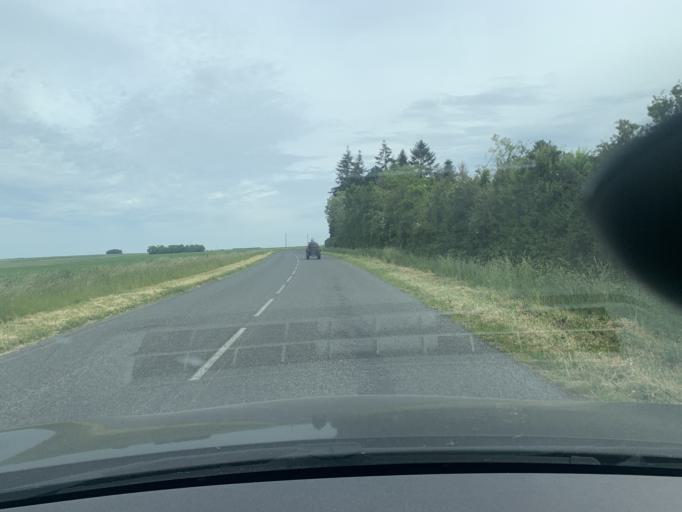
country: FR
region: Nord-Pas-de-Calais
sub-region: Departement du Nord
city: Masnieres
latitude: 50.1325
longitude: 3.1958
